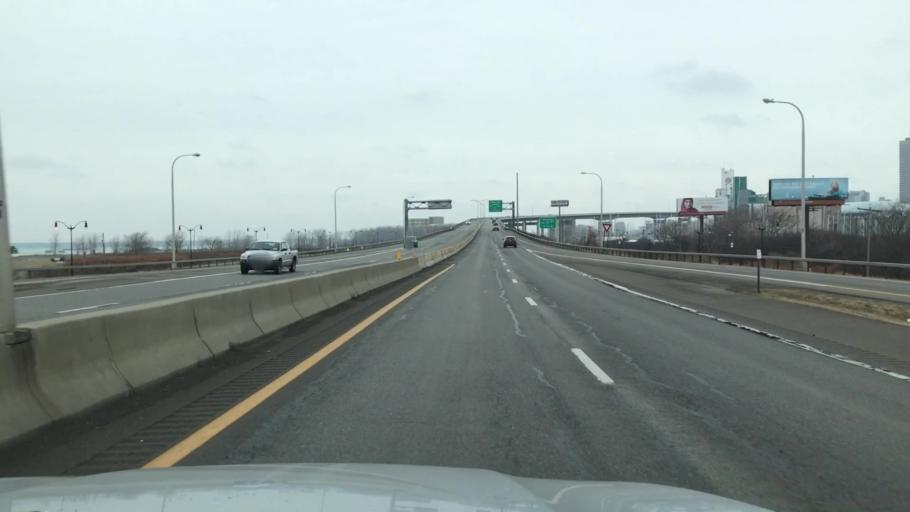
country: US
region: New York
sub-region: Erie County
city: Buffalo
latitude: 42.8647
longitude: -78.8751
